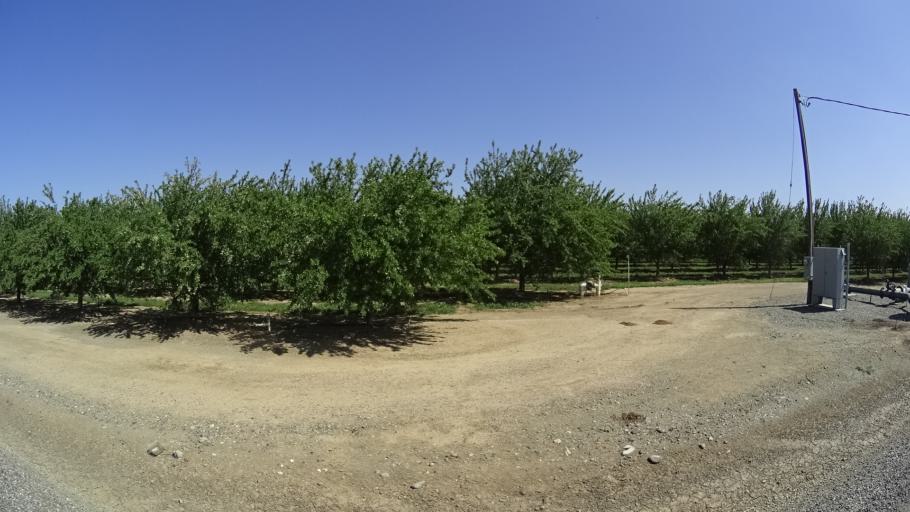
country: US
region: California
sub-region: Glenn County
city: Willows
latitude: 39.6229
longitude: -122.1375
